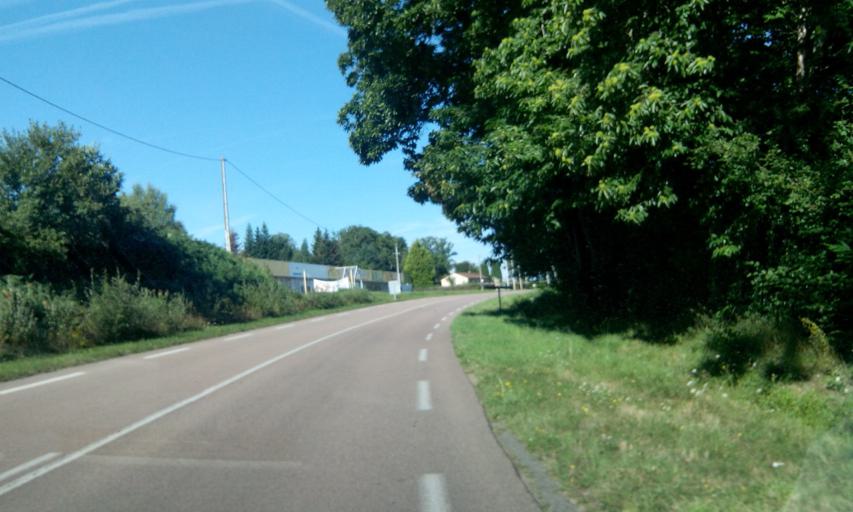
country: FR
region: Limousin
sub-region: Departement de la Haute-Vienne
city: Saint-Just-le-Martel
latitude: 45.8427
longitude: 1.4042
